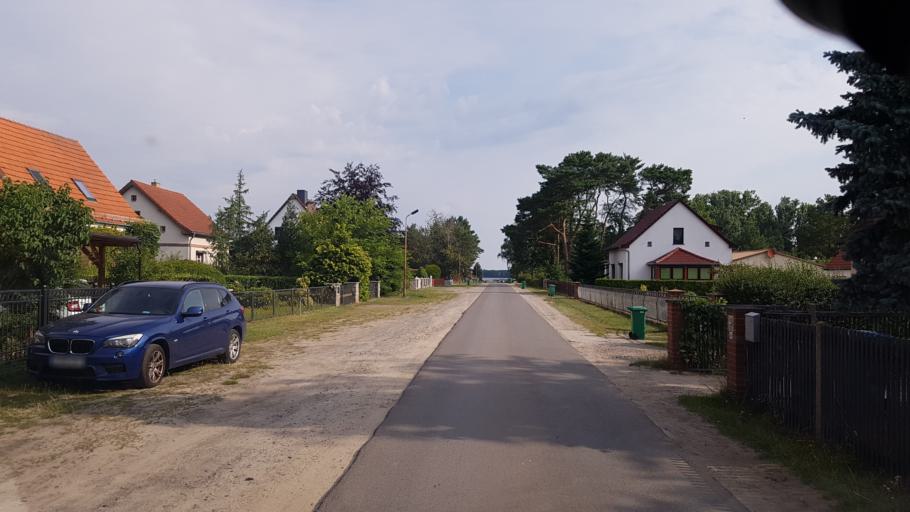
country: DE
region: Brandenburg
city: Gross Koris
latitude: 52.1657
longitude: 13.6939
